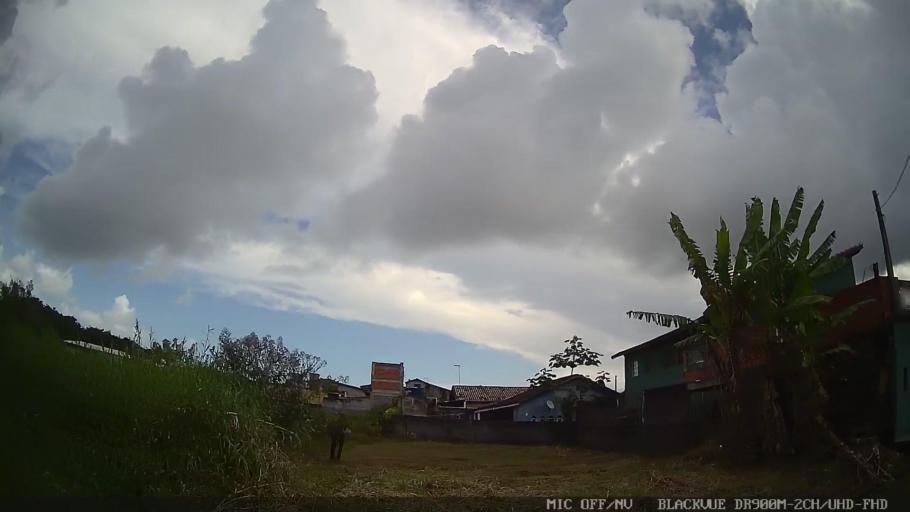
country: BR
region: Sao Paulo
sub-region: Itanhaem
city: Itanhaem
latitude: -24.2064
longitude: -46.8483
